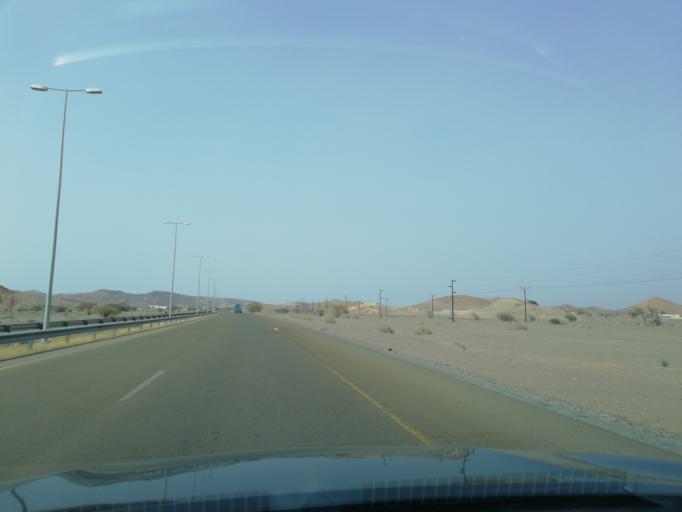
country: OM
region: Al Batinah
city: Al Liwa'
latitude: 24.3632
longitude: 56.5308
